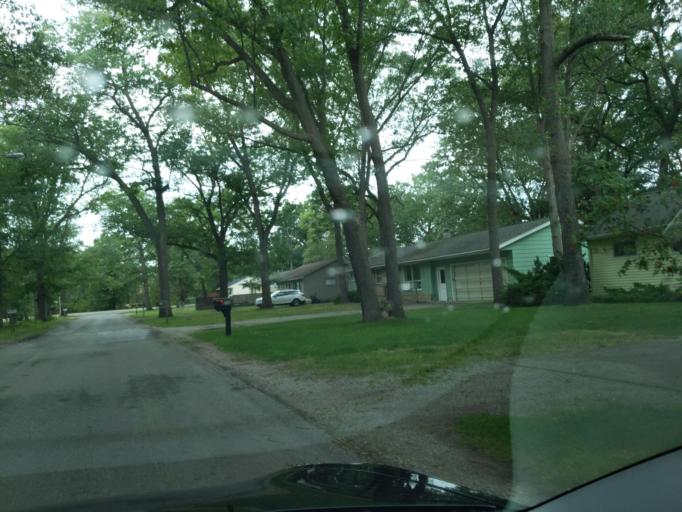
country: US
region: Michigan
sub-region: Grand Traverse County
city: Traverse City
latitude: 44.7506
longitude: -85.5729
